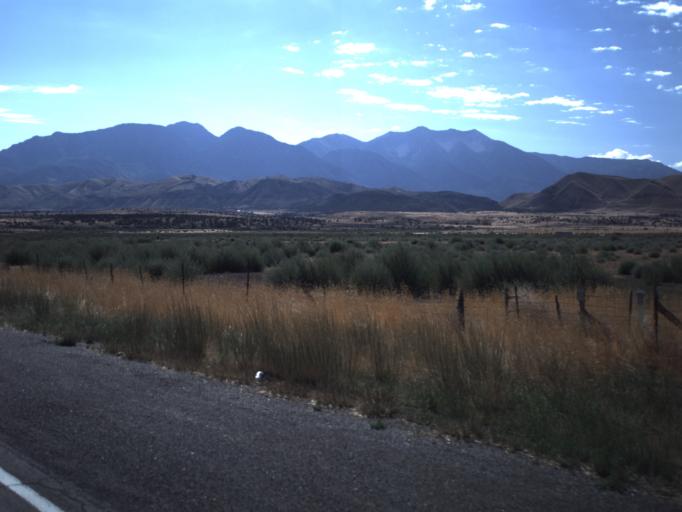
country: US
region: Utah
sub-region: Utah County
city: Genola
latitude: 39.9520
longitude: -111.9544
